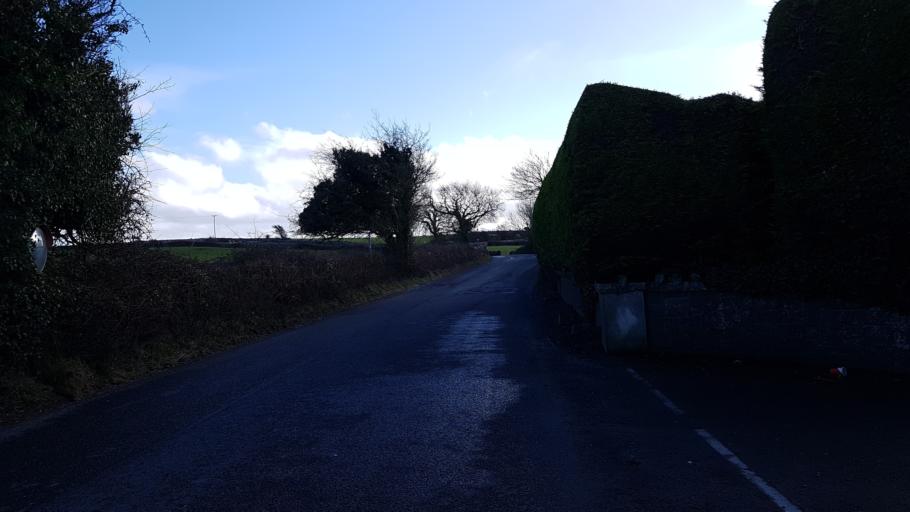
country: IE
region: Connaught
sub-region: County Galway
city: Gaillimh
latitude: 53.3087
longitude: -9.0205
